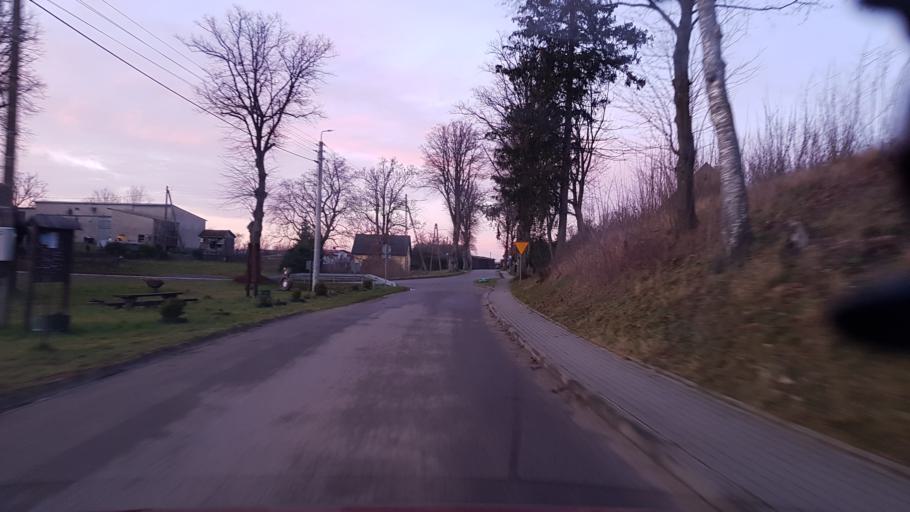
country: PL
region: Pomeranian Voivodeship
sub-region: Powiat bytowski
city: Tuchomie
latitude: 54.1330
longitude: 17.3641
